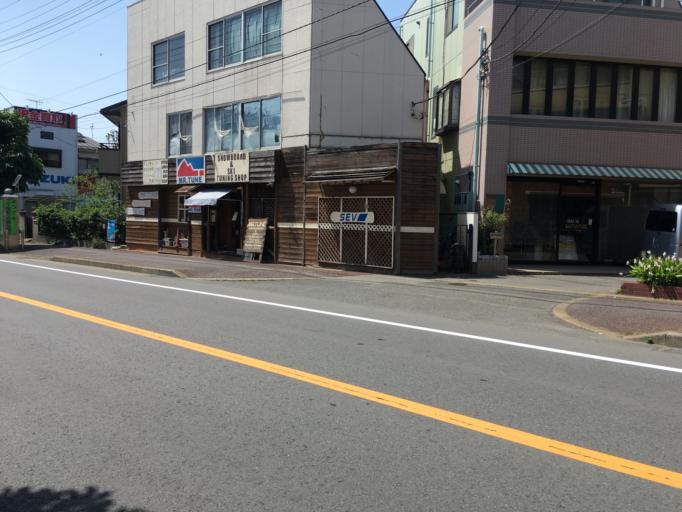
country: JP
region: Chiba
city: Matsudo
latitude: 35.7687
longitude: 139.9062
